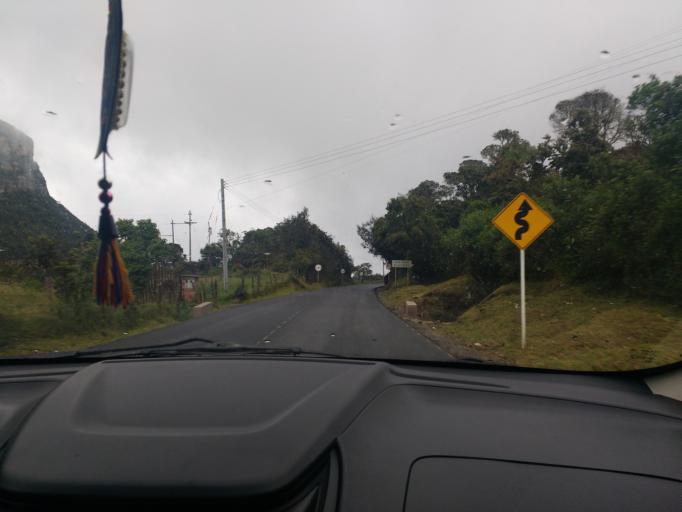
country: CO
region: Cundinamarca
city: Choachi
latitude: 4.5669
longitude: -73.9705
